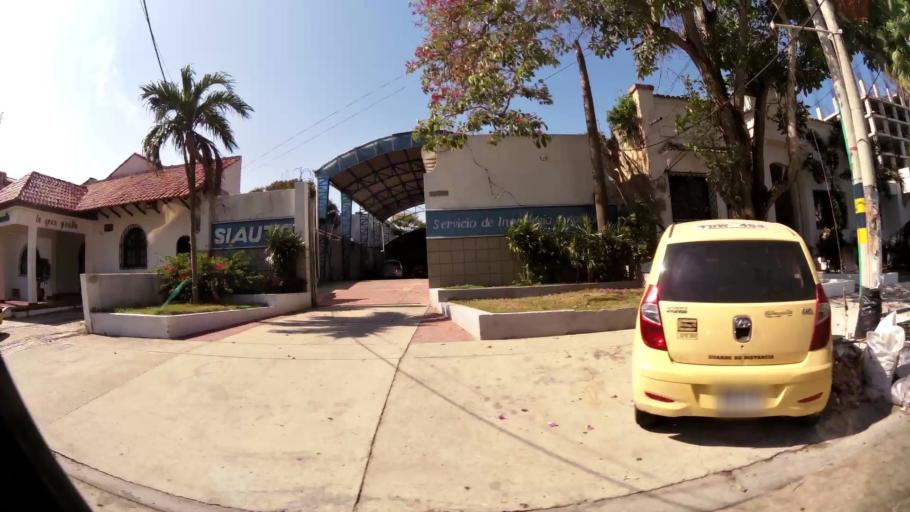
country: CO
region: Atlantico
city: Barranquilla
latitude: 10.9970
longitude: -74.8051
